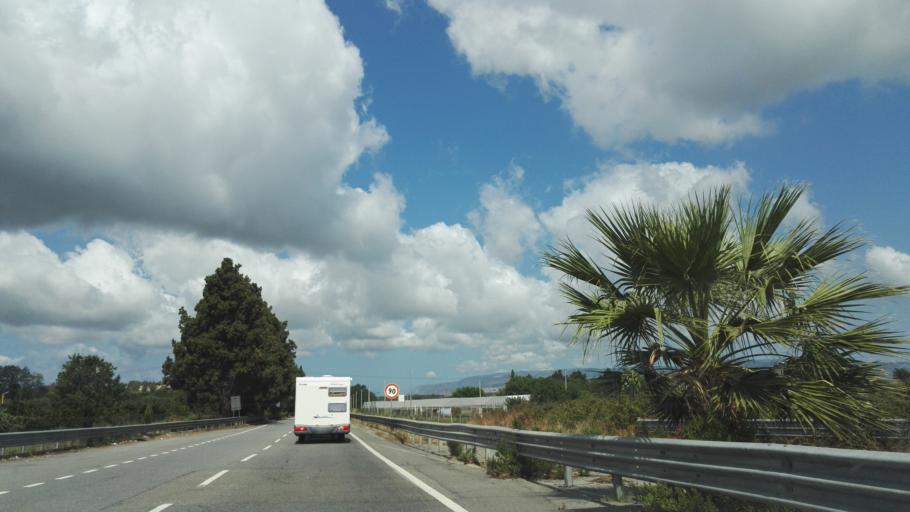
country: IT
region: Calabria
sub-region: Provincia di Reggio Calabria
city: Melicucco
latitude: 38.4585
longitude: 16.0205
